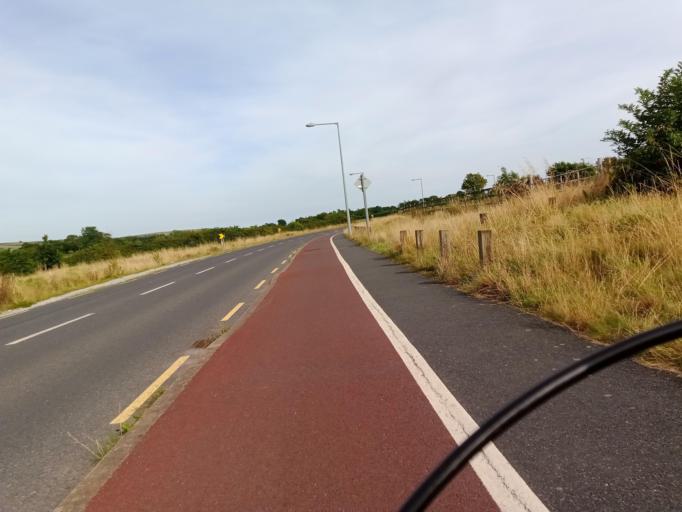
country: IE
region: Munster
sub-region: Waterford
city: Dungarvan
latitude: 52.1000
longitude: -7.5646
